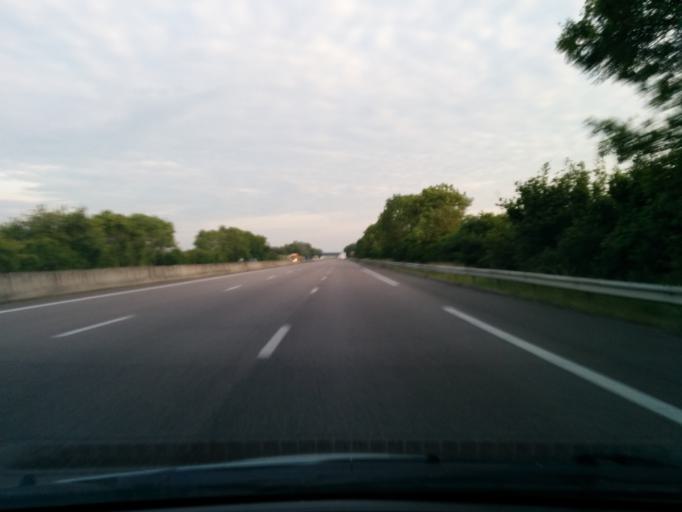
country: FR
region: Haute-Normandie
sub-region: Departement de l'Eure
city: La Chapelle-Reanville
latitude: 49.0747
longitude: 1.3996
